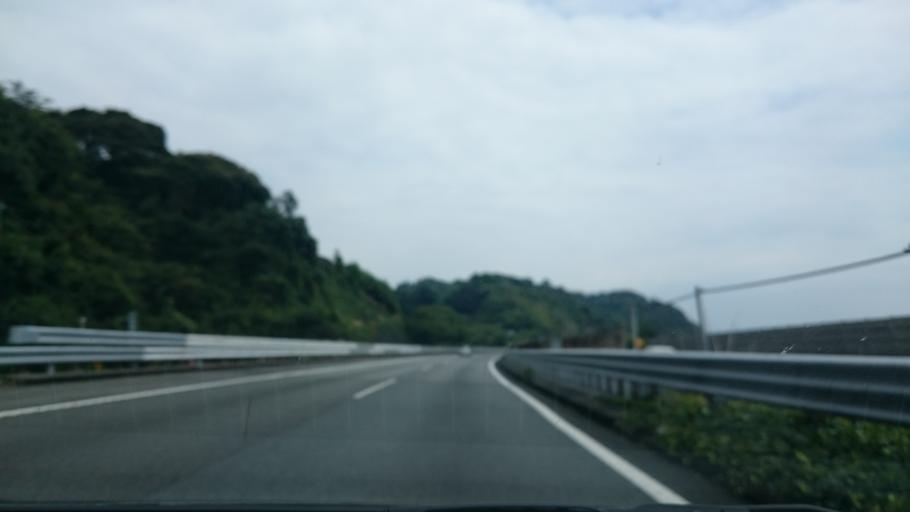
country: JP
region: Shizuoka
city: Fujinomiya
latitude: 35.1152
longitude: 138.5785
